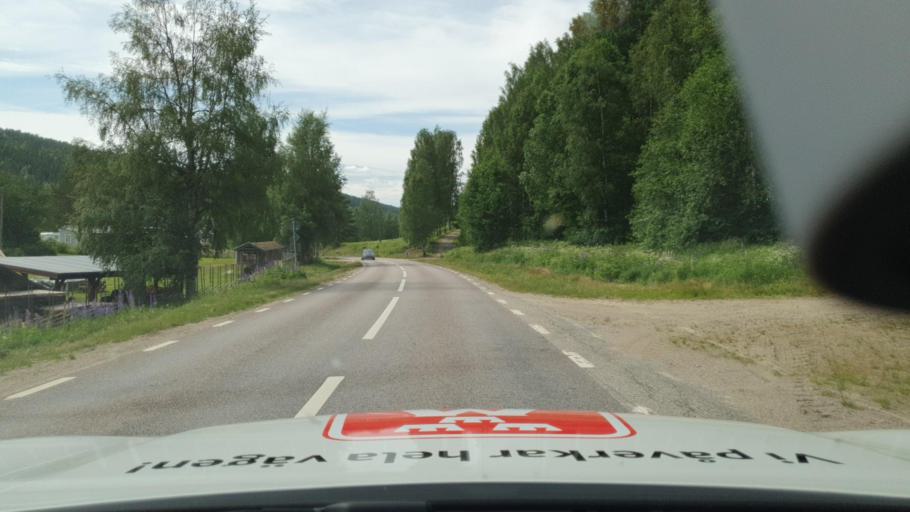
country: NO
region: Hedmark
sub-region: Trysil
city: Innbygda
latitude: 60.8849
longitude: 12.6495
